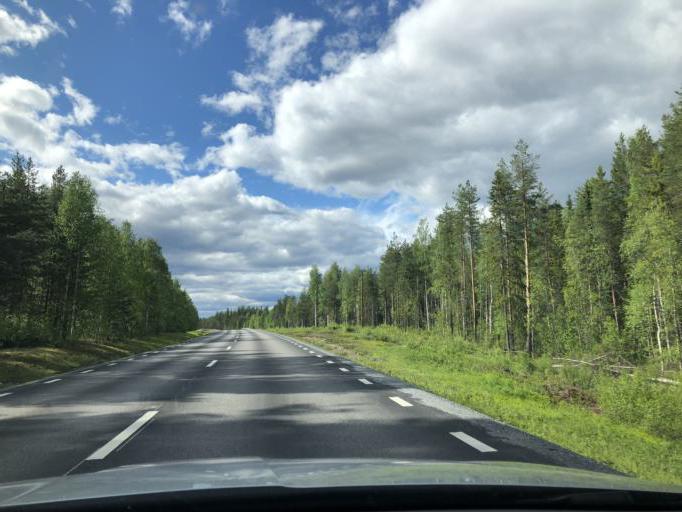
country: SE
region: Norrbotten
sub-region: Alvsbyns Kommun
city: AElvsbyn
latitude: 65.6833
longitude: 20.7355
